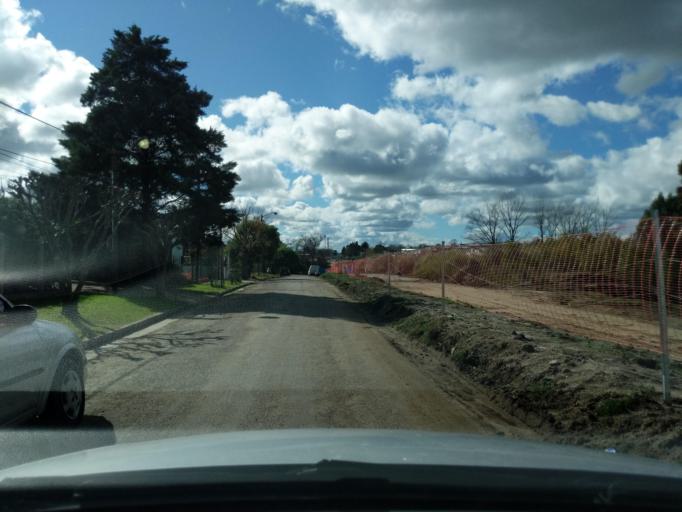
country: UY
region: Florida
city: Florida
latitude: -34.0937
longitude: -56.2260
